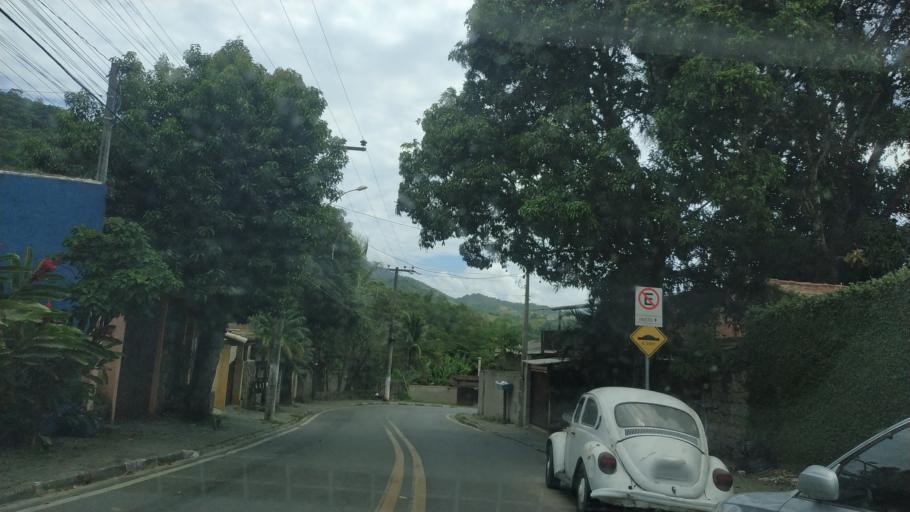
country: BR
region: Sao Paulo
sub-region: Ilhabela
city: Ilhabela
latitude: -23.8289
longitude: -45.3551
